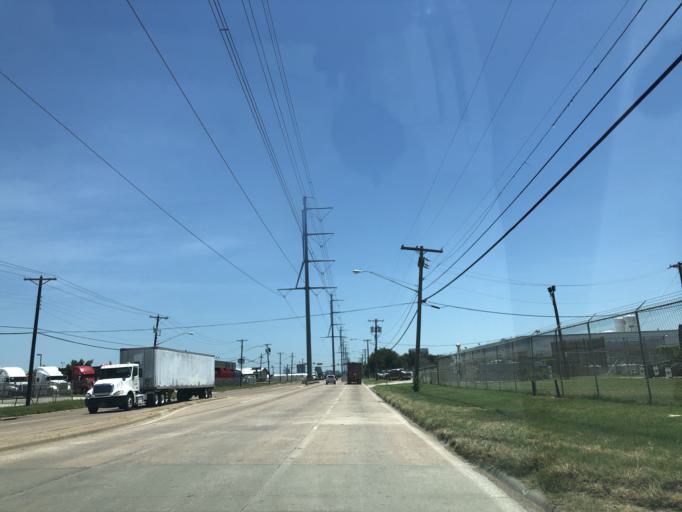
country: US
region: Texas
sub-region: Dallas County
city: Irving
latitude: 32.8081
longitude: -96.8921
